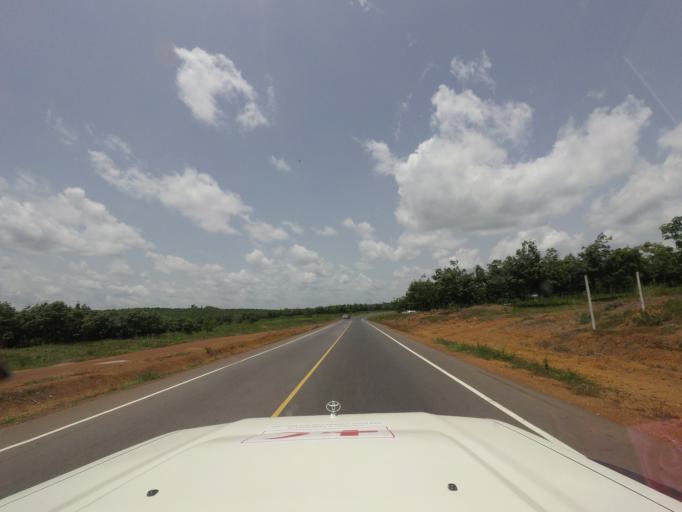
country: LR
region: Margibi
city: Kakata
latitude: 6.4497
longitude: -10.4383
